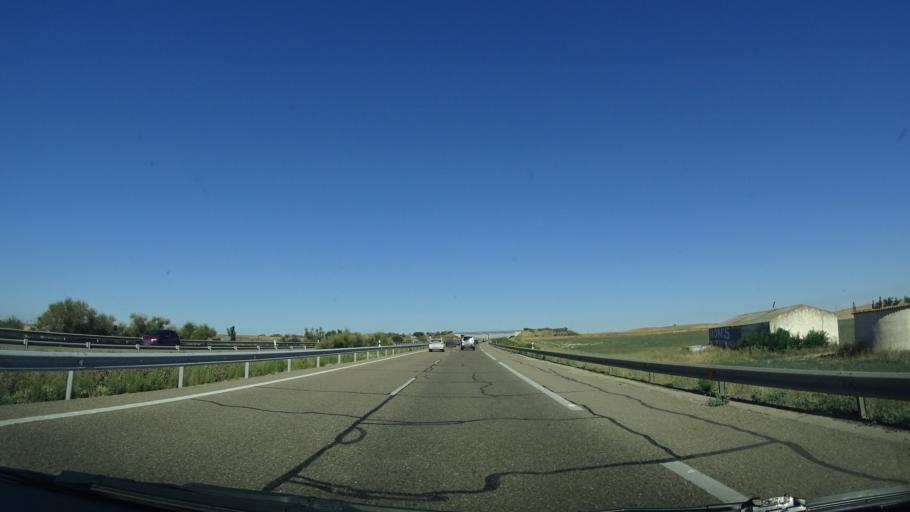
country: ES
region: Castille and Leon
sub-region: Provincia de Zamora
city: Cerecinos de Campos
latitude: 41.9053
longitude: -5.4906
